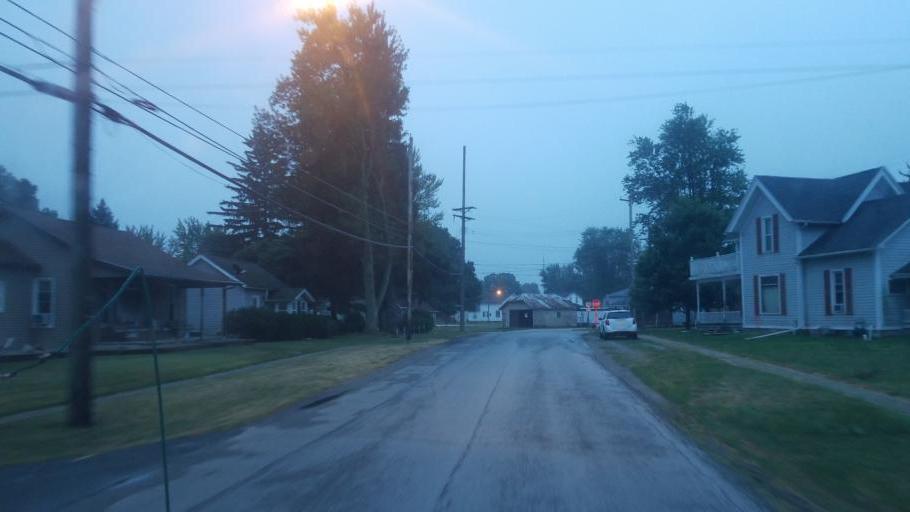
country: US
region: Ohio
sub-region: Defiance County
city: Hicksville
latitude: 41.2965
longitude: -84.7667
